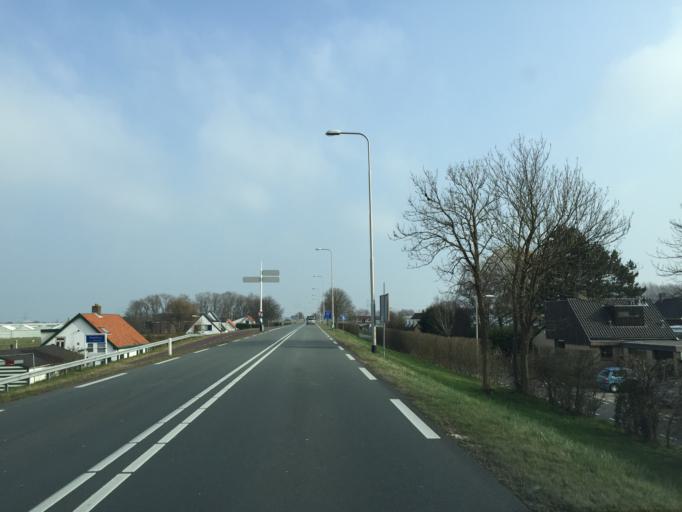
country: NL
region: South Holland
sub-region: Gemeente Westland
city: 's-Gravenzande
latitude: 51.9799
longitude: 4.1816
